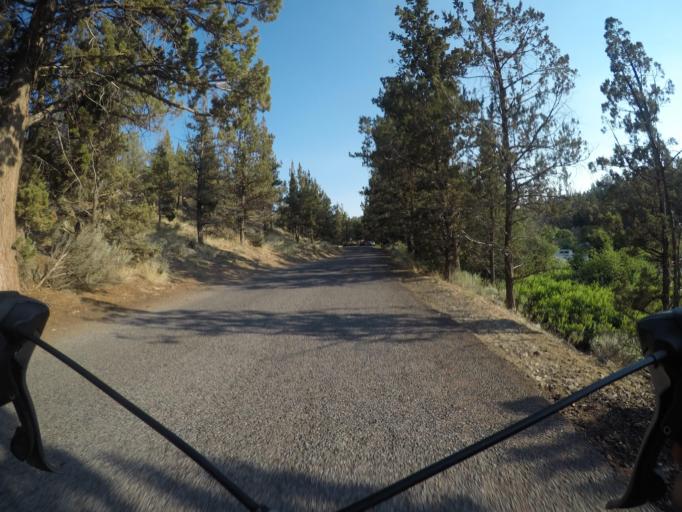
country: US
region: Oregon
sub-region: Deschutes County
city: Redmond
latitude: 44.2704
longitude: -121.2564
